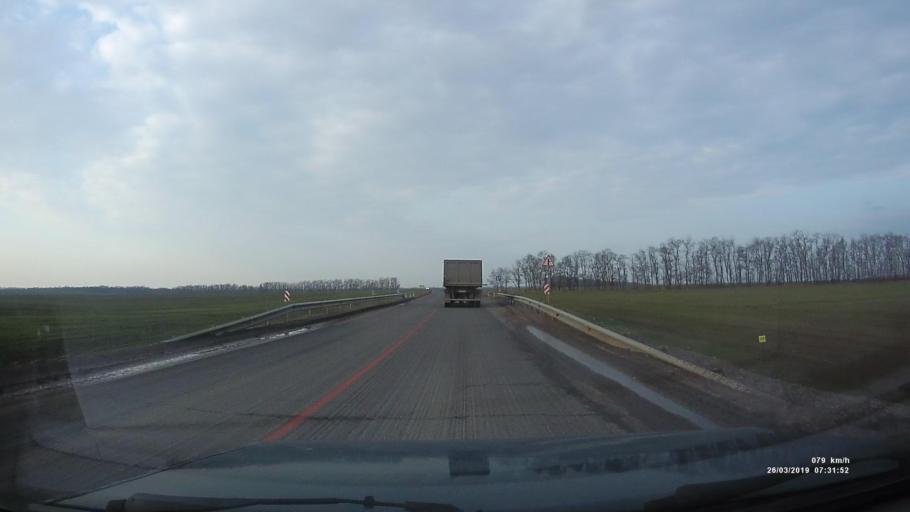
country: RU
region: Rostov
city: Novobessergenovka
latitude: 47.2306
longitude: 38.7844
